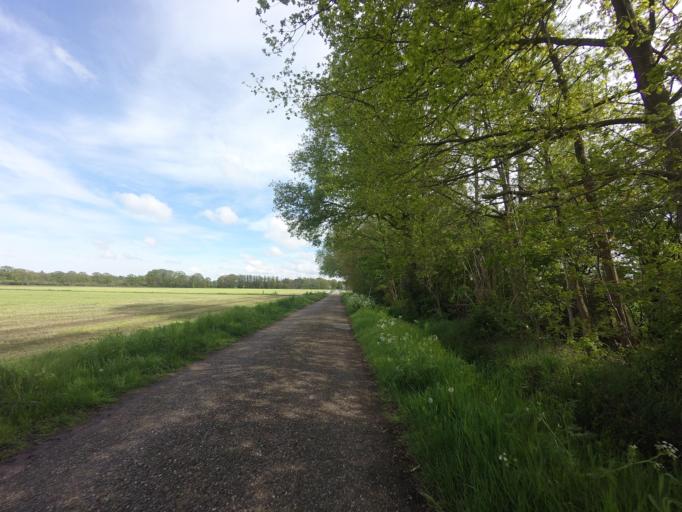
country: NL
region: Overijssel
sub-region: Gemeente Enschede
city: Enschede
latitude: 52.1875
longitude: 6.8264
